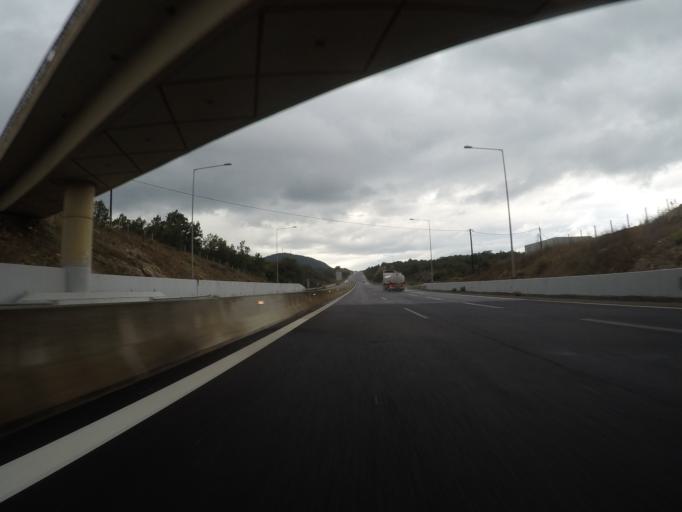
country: GR
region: Peloponnese
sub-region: Nomos Arkadias
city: Megalopoli
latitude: 37.3312
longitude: 22.0774
